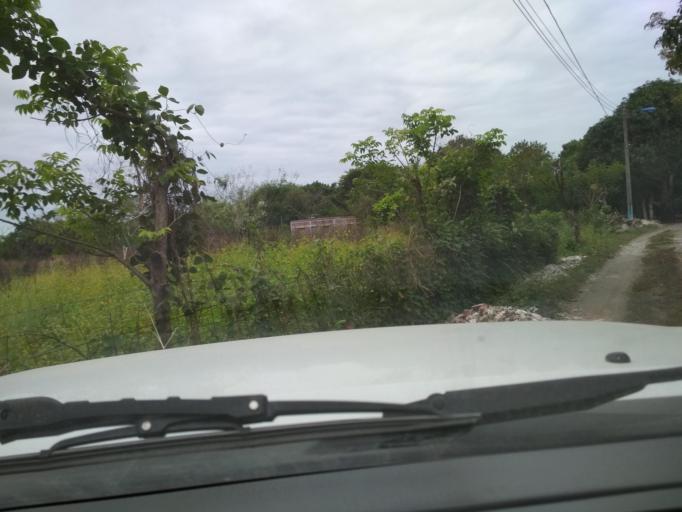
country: MX
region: Veracruz
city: El Tejar
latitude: 19.0725
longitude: -96.1352
